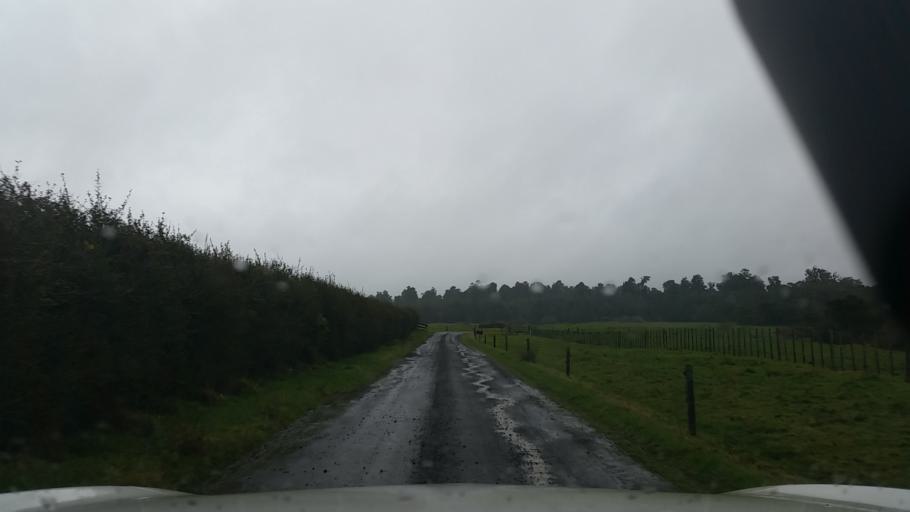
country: NZ
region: Taranaki
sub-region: South Taranaki District
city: Eltham
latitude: -39.2799
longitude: 174.1797
